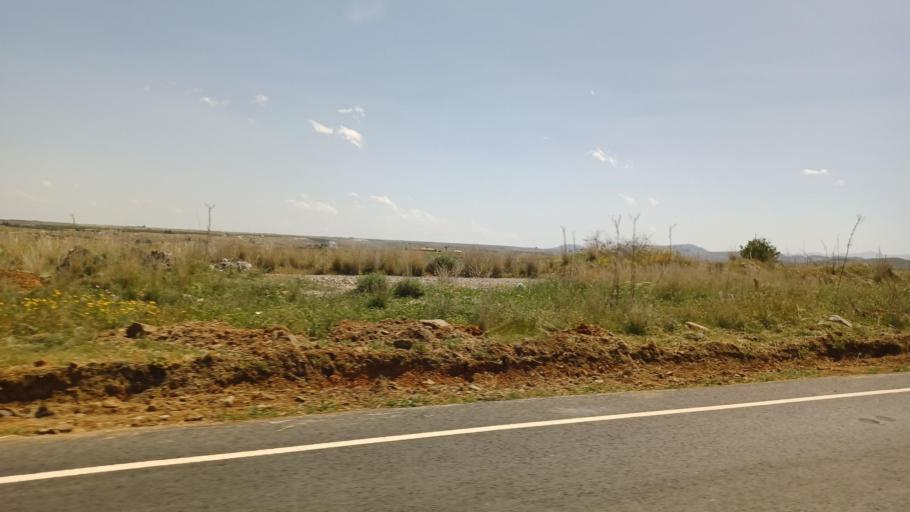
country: CY
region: Lefkosia
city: Astromeritis
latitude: 35.1066
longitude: 33.0151
